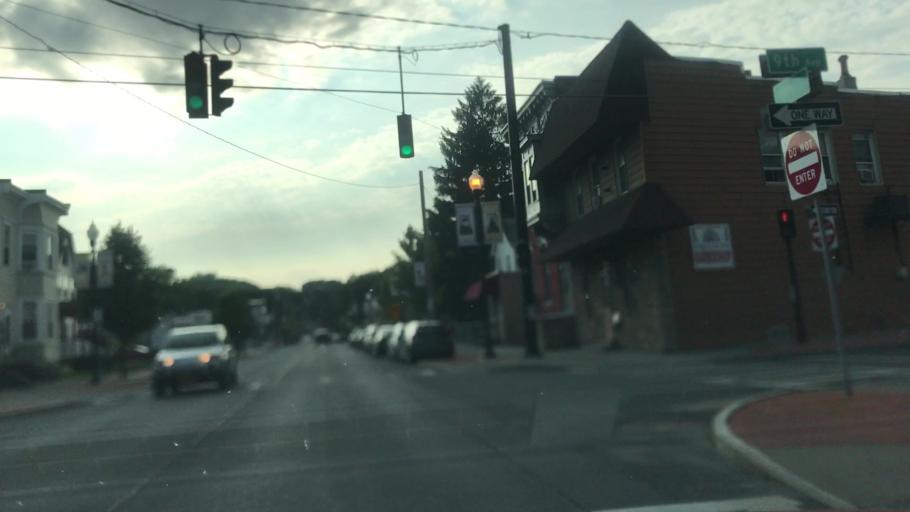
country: US
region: New York
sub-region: Albany County
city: Watervliet
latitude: 42.7322
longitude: -73.7088
